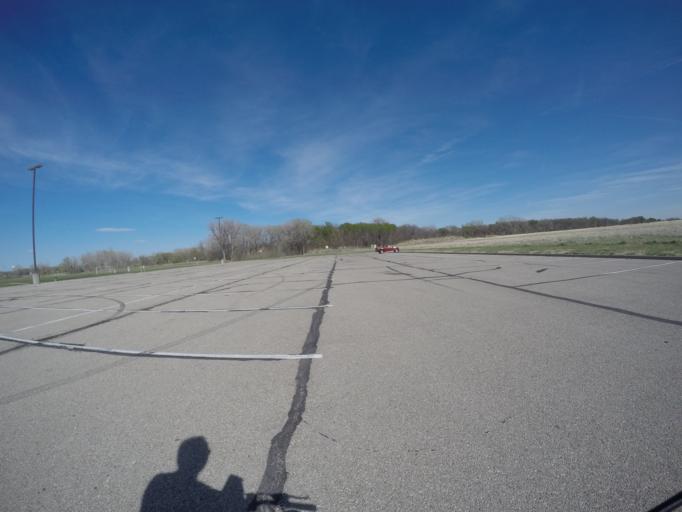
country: US
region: Kansas
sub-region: Saline County
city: Salina
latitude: 38.7949
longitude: -97.5768
